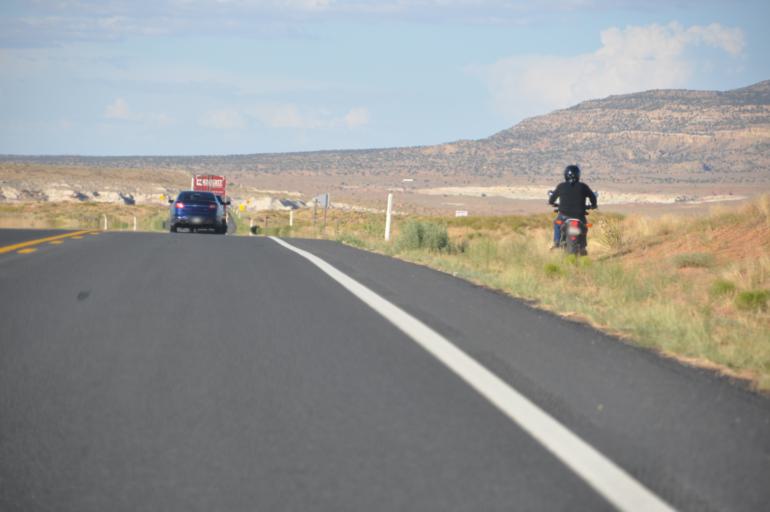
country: US
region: Arizona
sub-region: Coconino County
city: Kaibito
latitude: 36.3103
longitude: -110.9619
